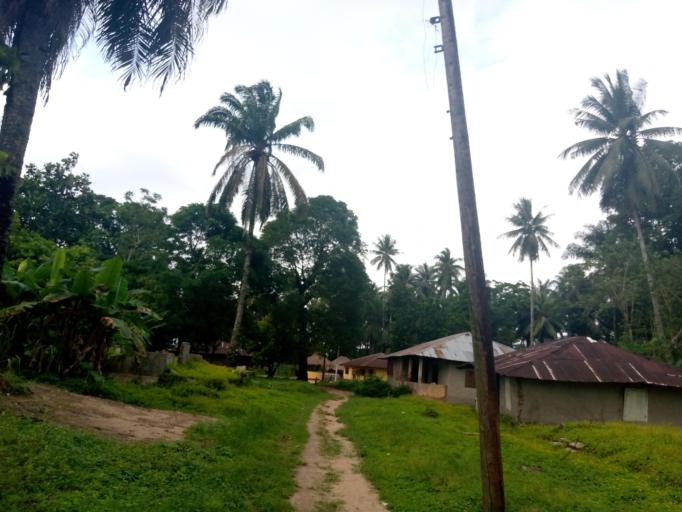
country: SL
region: Southern Province
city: Bonthe
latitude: 7.5219
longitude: -12.5019
